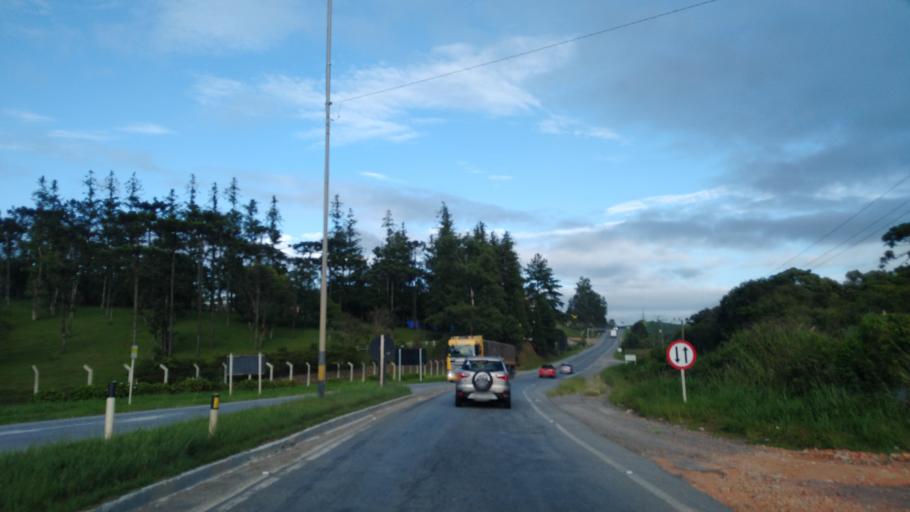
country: BR
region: Santa Catarina
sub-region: Rio Negrinho
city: Rio Negrinho
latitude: -26.2452
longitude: -49.4617
